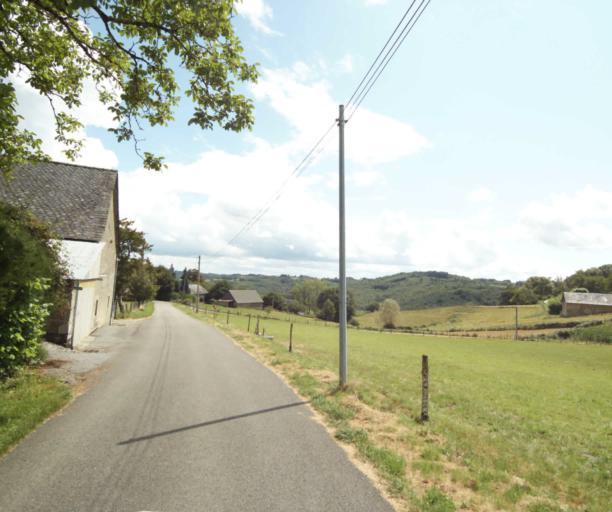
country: FR
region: Limousin
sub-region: Departement de la Correze
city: Sainte-Fortunade
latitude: 45.1743
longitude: 1.8306
